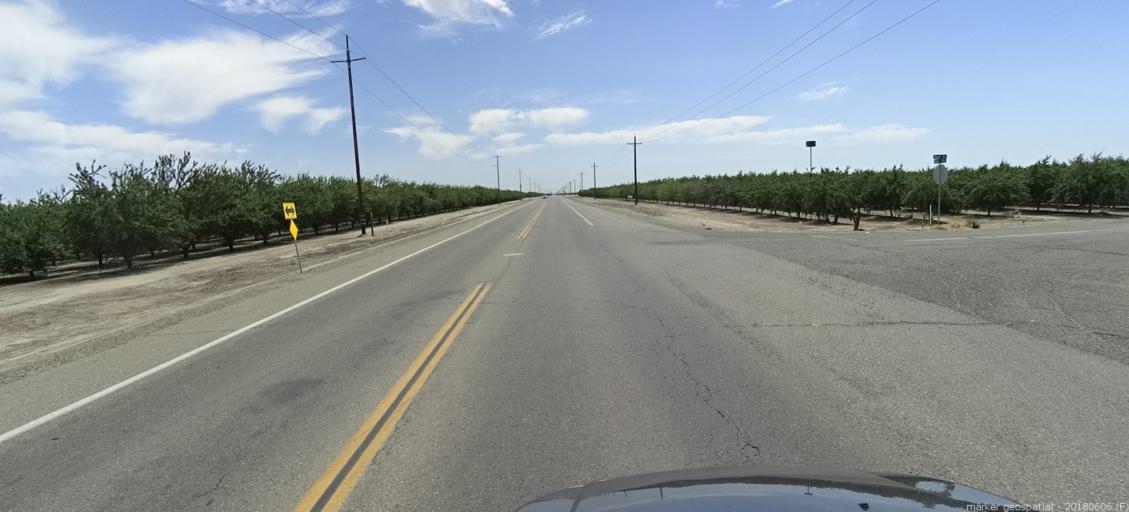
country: US
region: California
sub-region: Fresno County
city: Firebaugh
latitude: 36.8586
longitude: -120.3909
